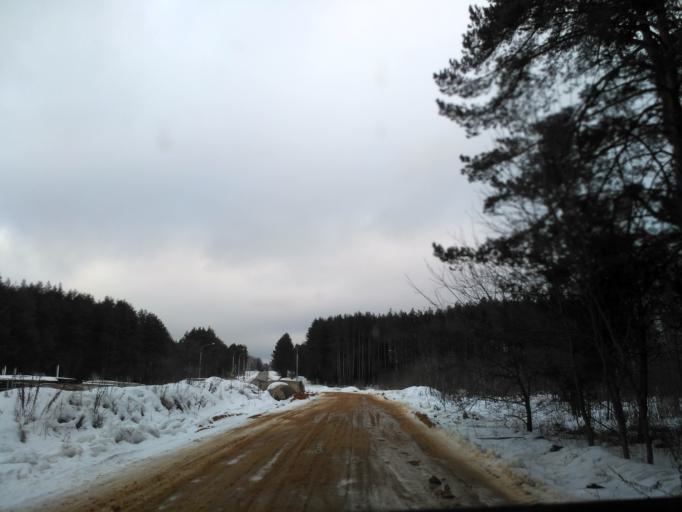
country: BY
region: Minsk
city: Lyeskawka
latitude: 53.9308
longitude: 27.7082
